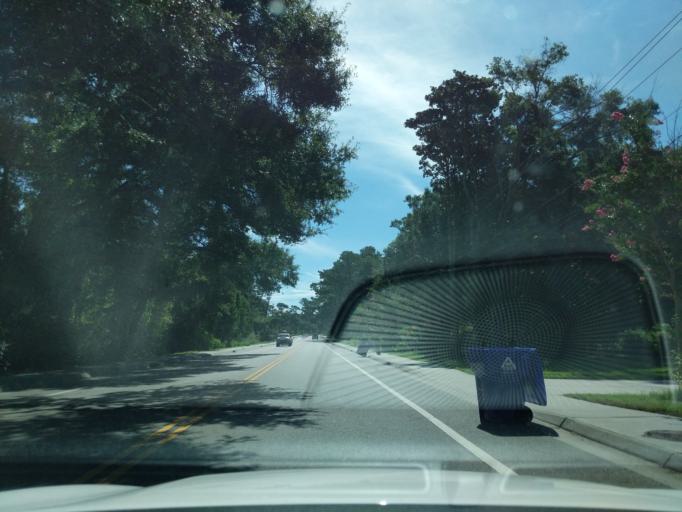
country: US
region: South Carolina
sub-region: Charleston County
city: Charleston
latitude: 32.7417
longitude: -79.9191
